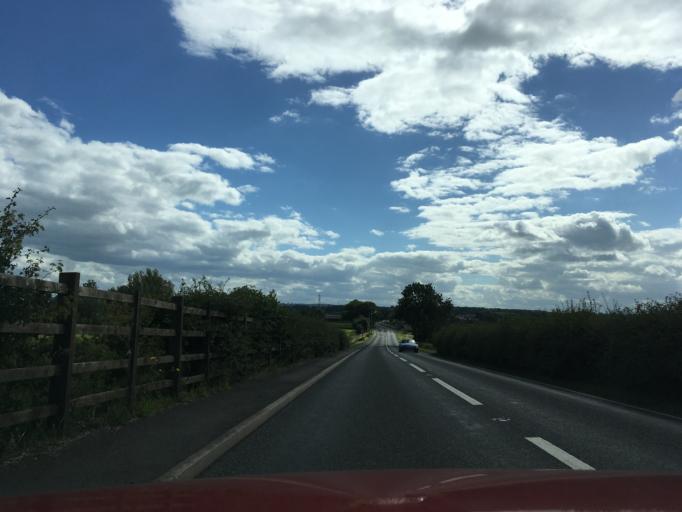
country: GB
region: England
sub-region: Nottinghamshire
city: Sutton Bonington
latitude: 52.8109
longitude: -1.2383
